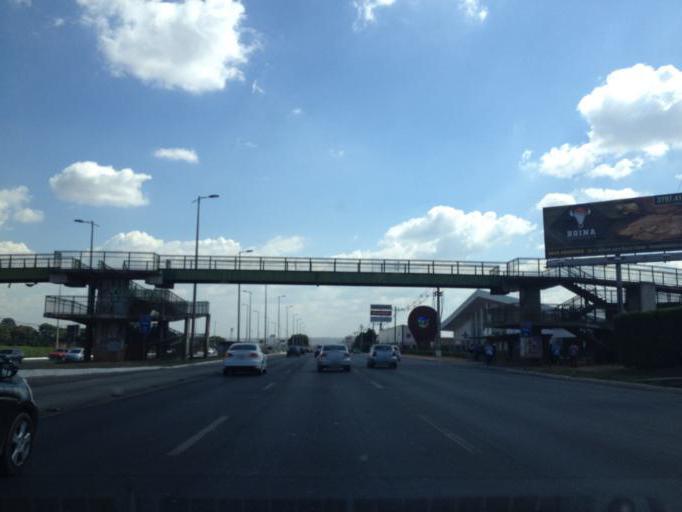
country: BR
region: Federal District
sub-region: Brasilia
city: Brasilia
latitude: -15.8087
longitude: -47.9570
